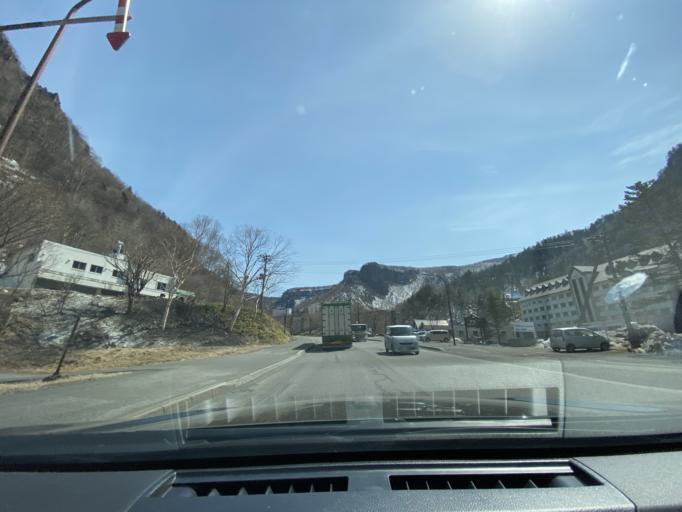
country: JP
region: Hokkaido
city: Kamikawa
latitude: 43.7303
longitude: 142.9427
